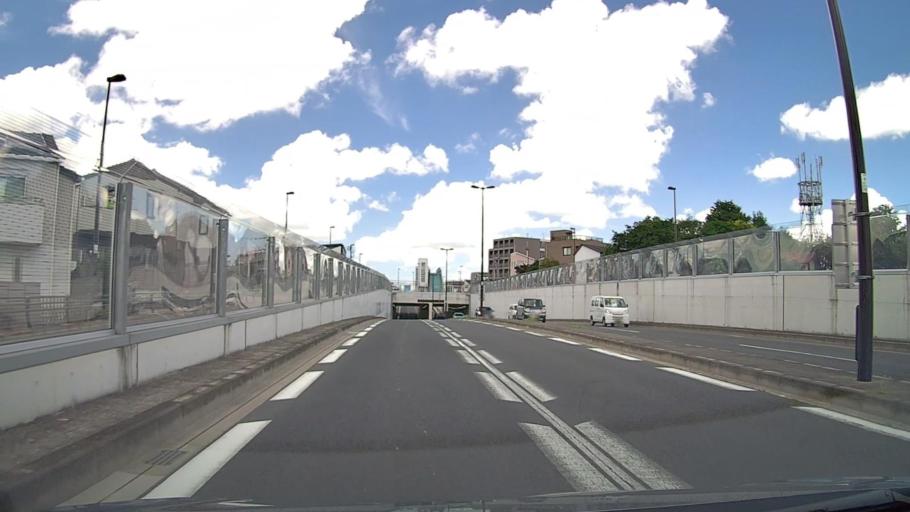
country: JP
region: Tokyo
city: Nishi-Tokyo-shi
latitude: 35.7455
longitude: 139.5581
